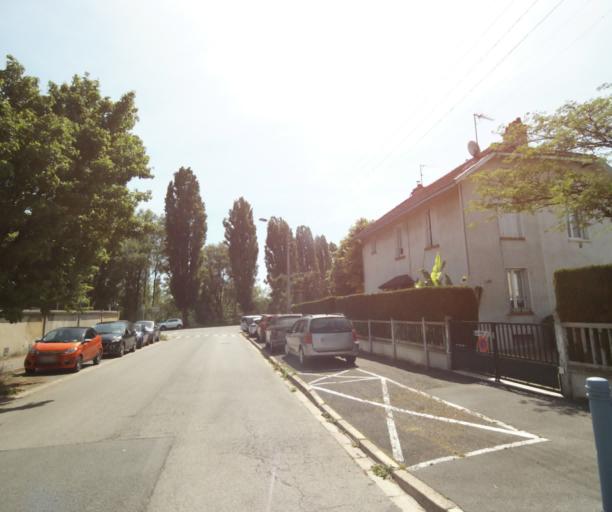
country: FR
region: Champagne-Ardenne
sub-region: Departement des Ardennes
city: Prix-les-Mezieres
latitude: 49.7617
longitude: 4.6947
